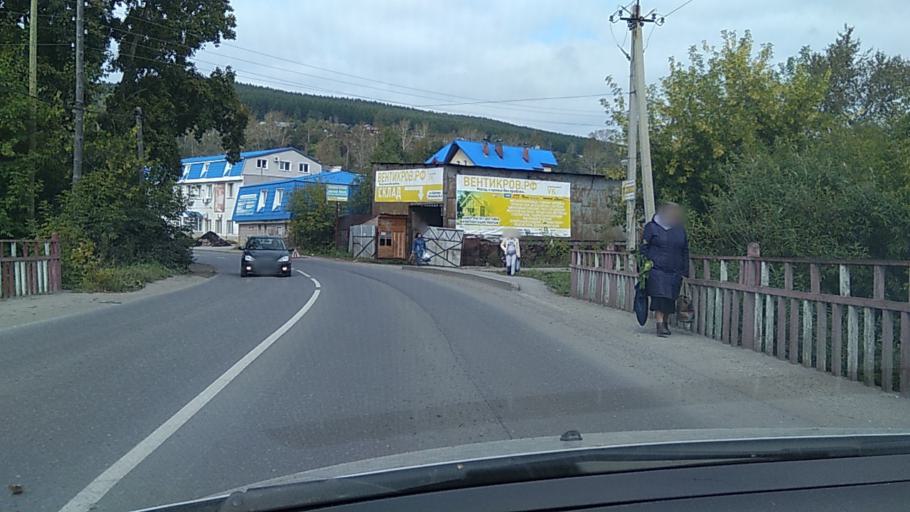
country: RU
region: Chelyabinsk
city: Zlatoust
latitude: 55.1770
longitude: 59.7040
